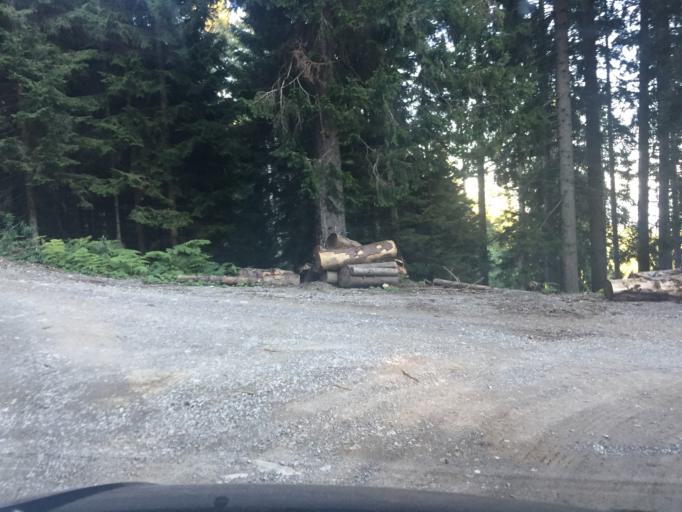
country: SI
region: Ravne na Koroskem
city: Kotlje
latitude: 46.4796
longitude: 14.9809
